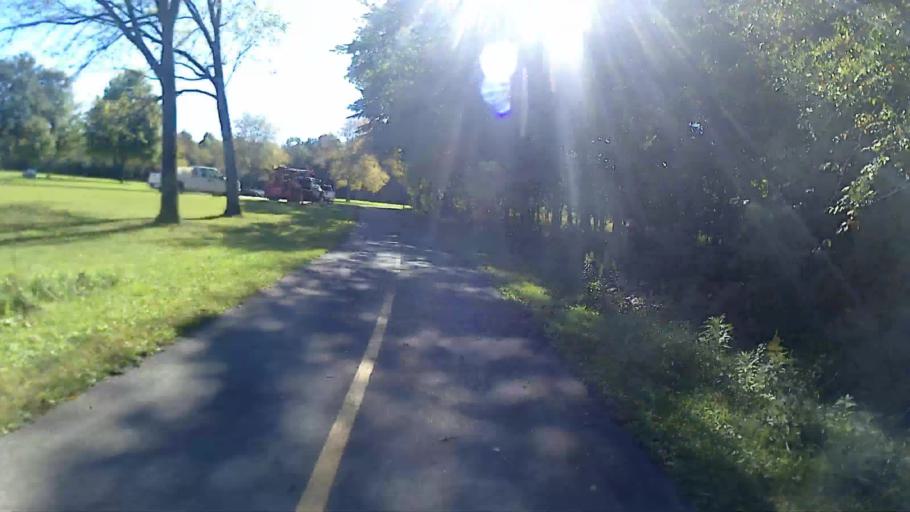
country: US
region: Illinois
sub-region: Cook County
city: Elk Grove Village
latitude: 42.0153
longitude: -87.9990
